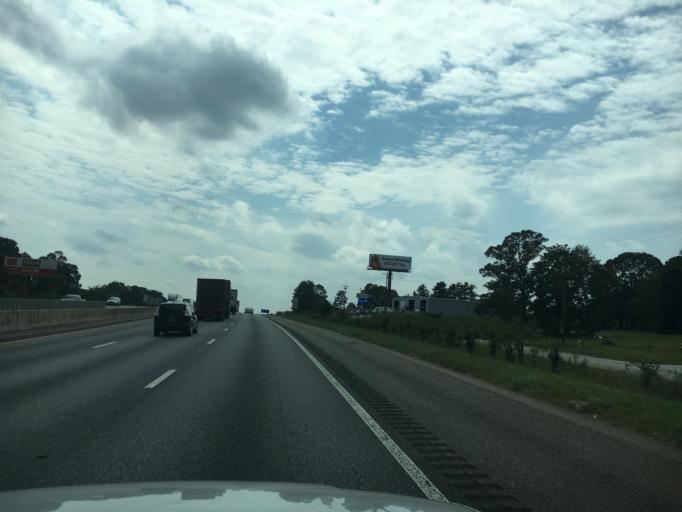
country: US
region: South Carolina
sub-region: Anderson County
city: Powdersville
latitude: 34.7692
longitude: -82.4694
